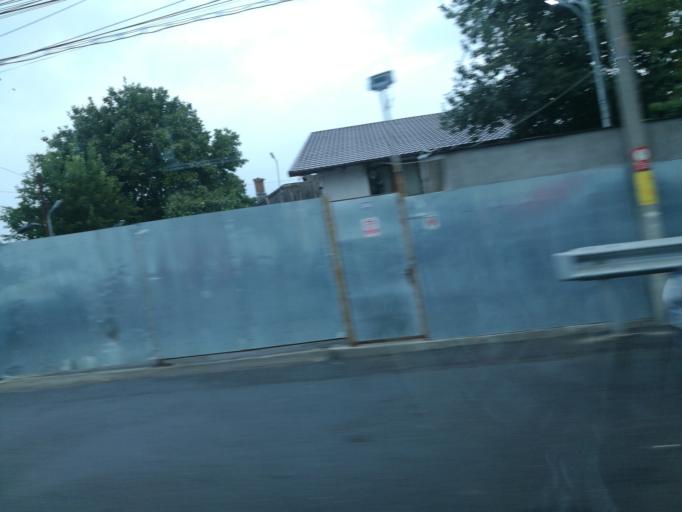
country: RO
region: Galati
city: Galati
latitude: 45.4670
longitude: 28.0349
